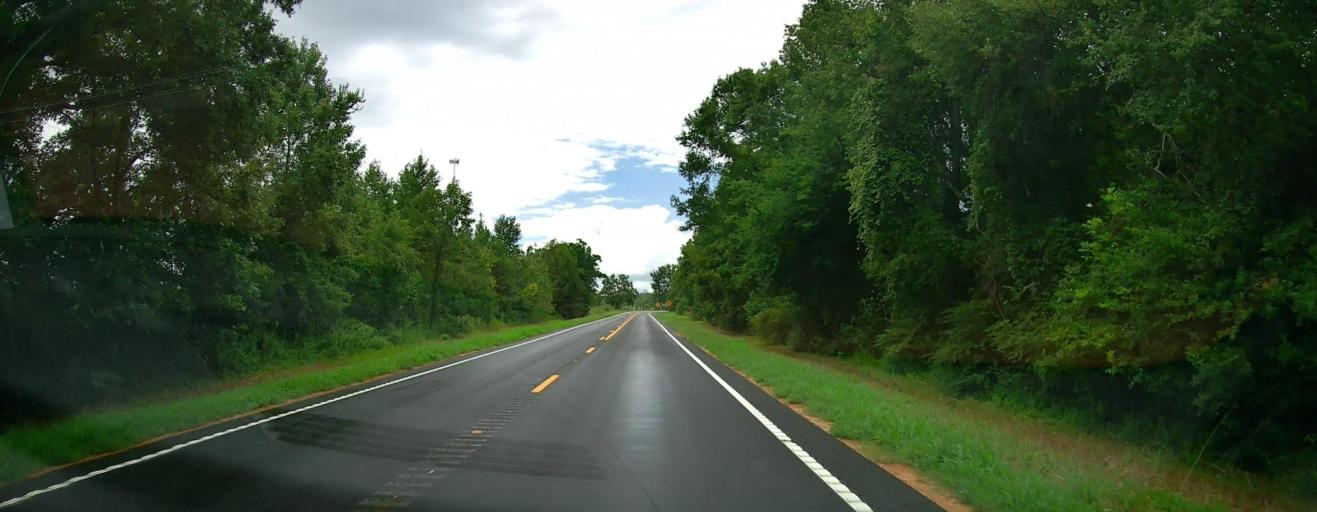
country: US
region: Georgia
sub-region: Wilcox County
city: Rochelle
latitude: 32.0988
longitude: -83.5839
